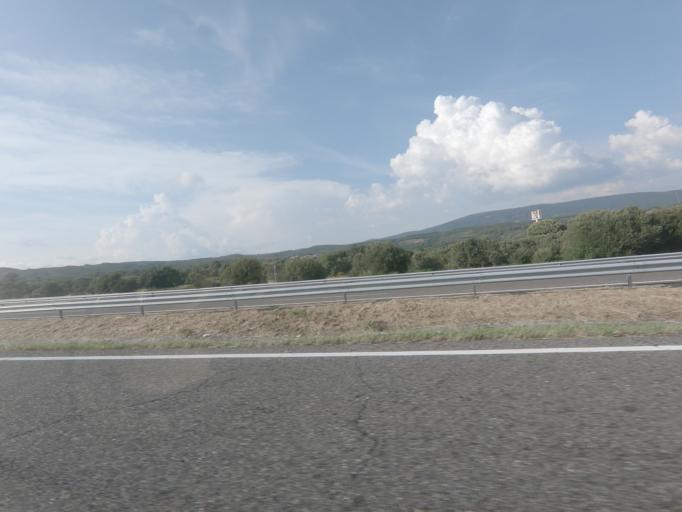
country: ES
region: Galicia
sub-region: Provincia de Ourense
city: Cualedro
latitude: 41.9821
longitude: -7.5440
